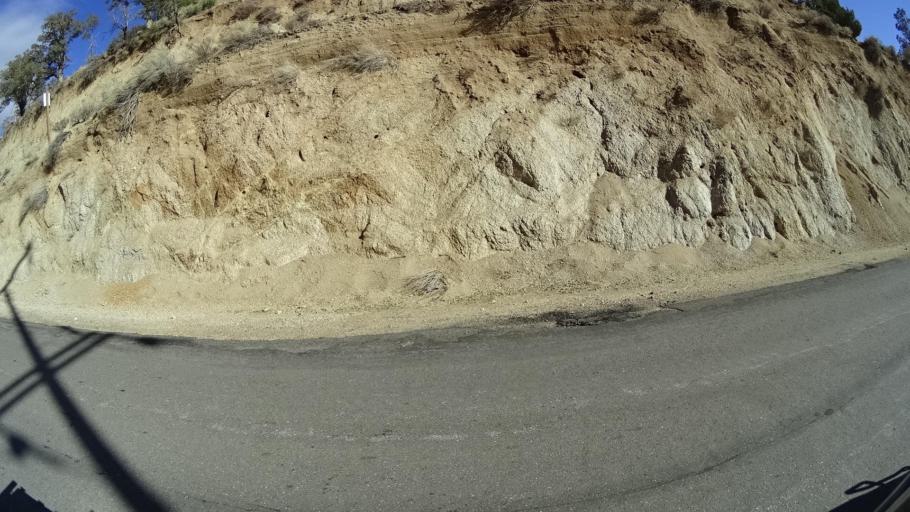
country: US
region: California
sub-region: Kern County
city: Bodfish
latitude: 35.5687
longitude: -118.5070
